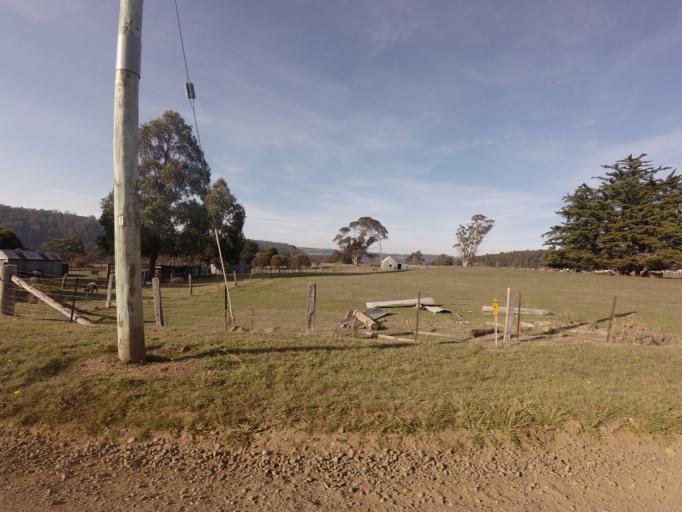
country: AU
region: Tasmania
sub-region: Brighton
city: Bridgewater
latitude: -42.4796
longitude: 147.3847
